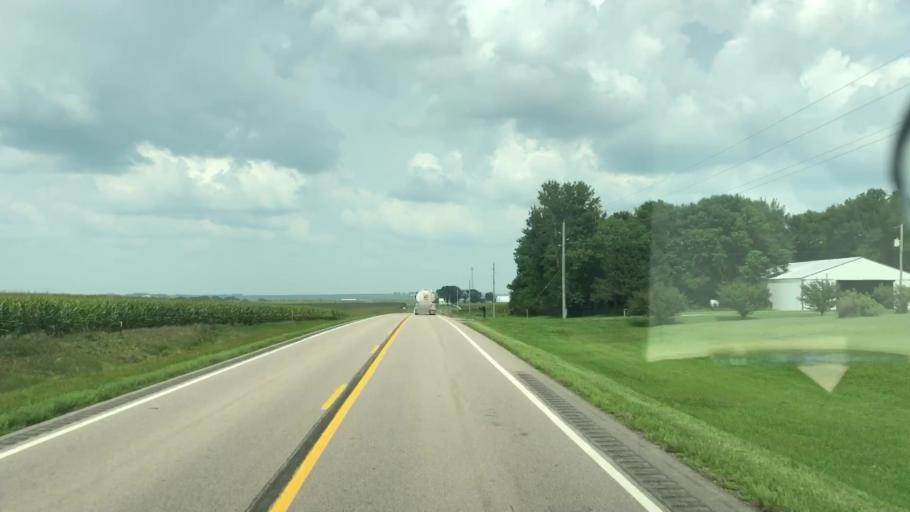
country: US
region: Iowa
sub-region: Plymouth County
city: Remsen
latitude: 42.7970
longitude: -95.9577
